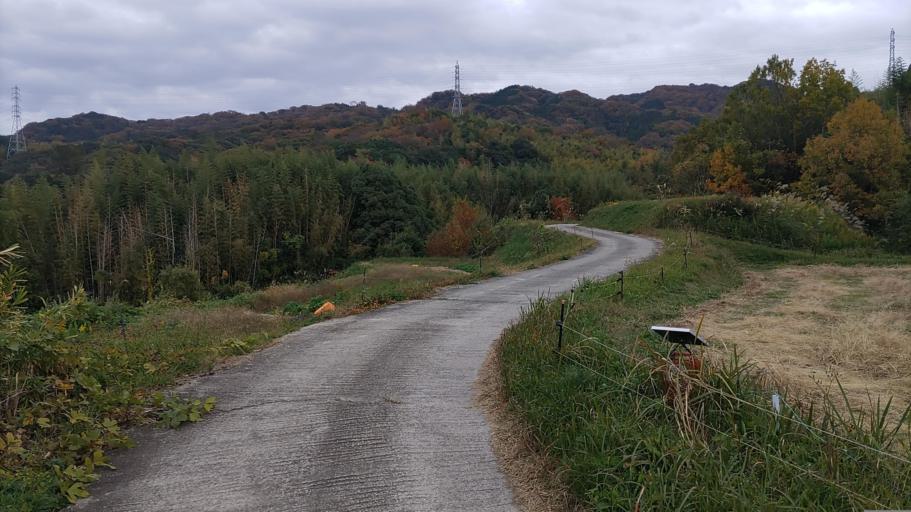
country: JP
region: Hyogo
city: Sumoto
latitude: 34.3836
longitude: 134.8167
